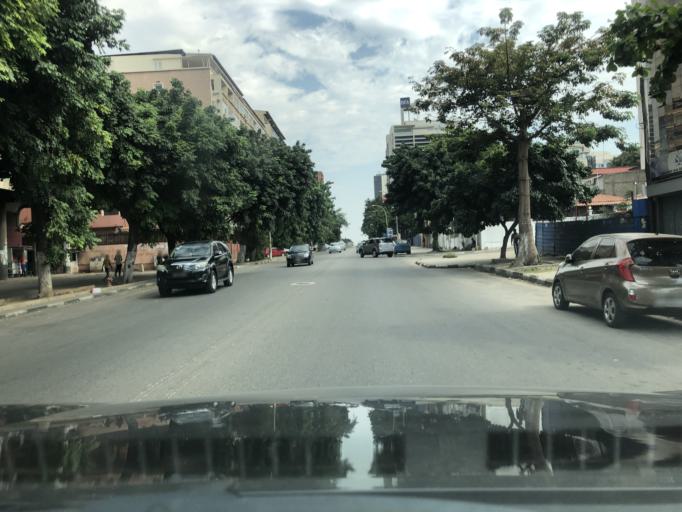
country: AO
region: Luanda
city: Luanda
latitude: -8.8207
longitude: 13.2302
